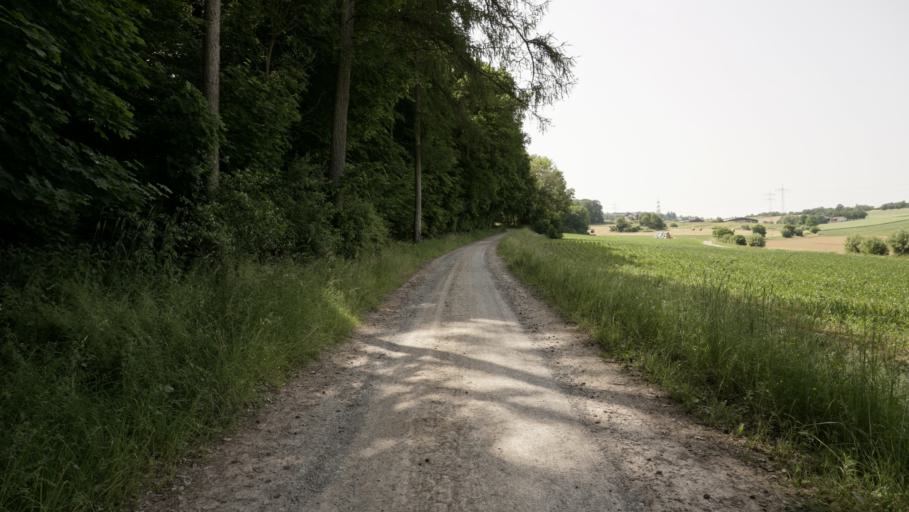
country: DE
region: Baden-Wuerttemberg
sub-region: Karlsruhe Region
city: Billigheim
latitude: 49.3407
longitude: 9.2201
